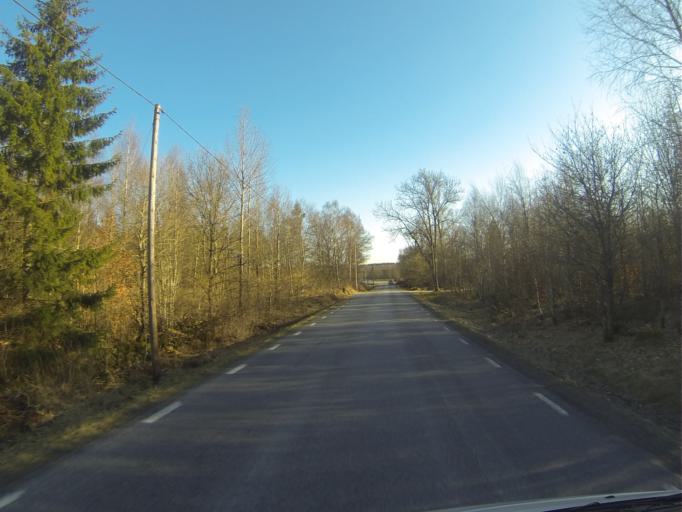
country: SE
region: Skane
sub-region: Horby Kommun
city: Hoerby
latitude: 55.8985
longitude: 13.6619
